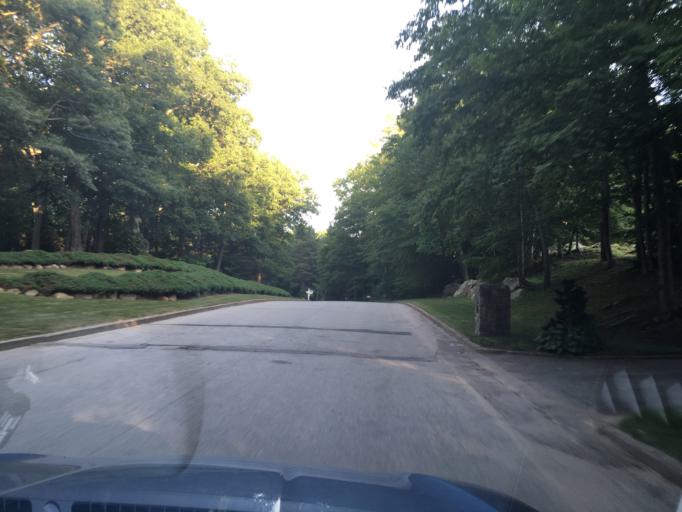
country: US
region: Rhode Island
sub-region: Washington County
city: Exeter
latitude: 41.6345
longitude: -71.5176
